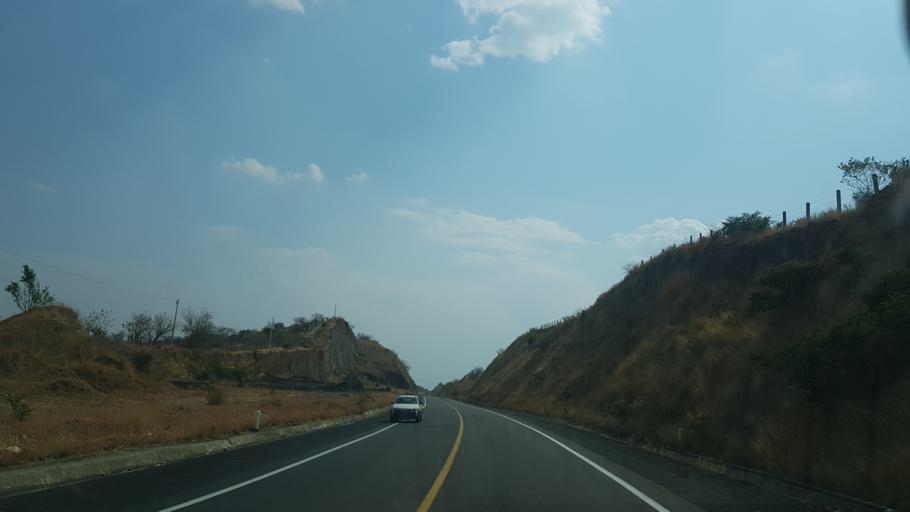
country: MX
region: Morelos
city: Tlacotepec
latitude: 18.8092
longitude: -98.7035
